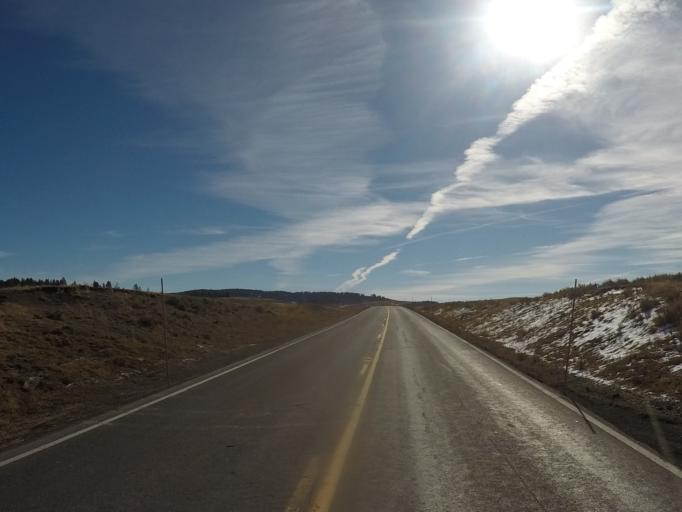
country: US
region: Montana
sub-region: Gallatin County
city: West Yellowstone
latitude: 44.6769
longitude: -110.4848
